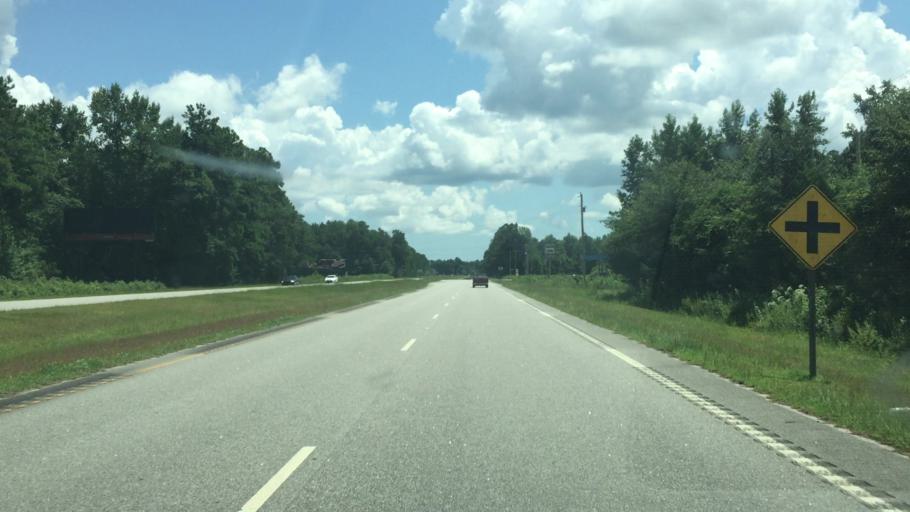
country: US
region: South Carolina
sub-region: Horry County
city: Loris
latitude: 34.0270
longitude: -78.8005
